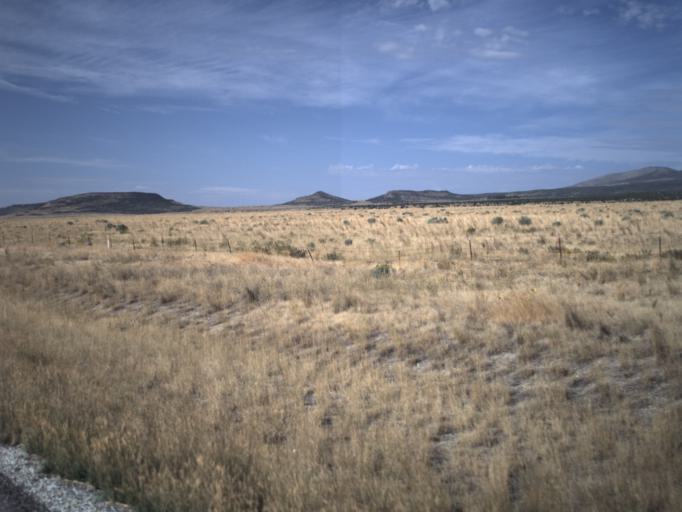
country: US
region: Idaho
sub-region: Oneida County
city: Malad City
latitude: 41.8892
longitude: -113.1128
